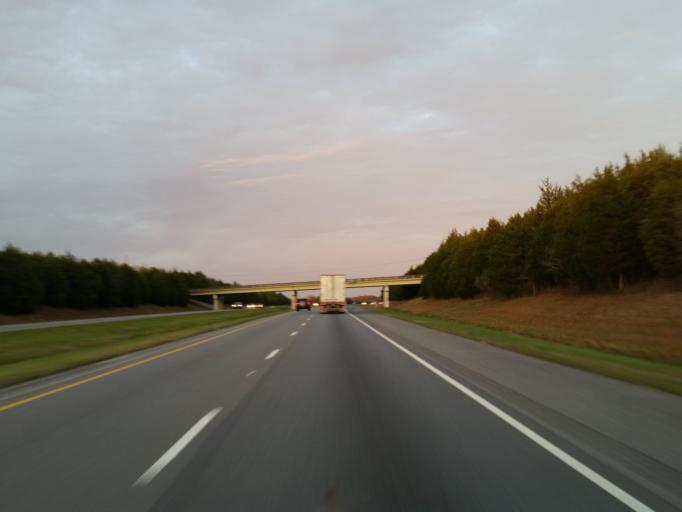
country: US
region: Alabama
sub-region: Sumter County
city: Livingston
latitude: 32.6789
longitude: -88.1654
